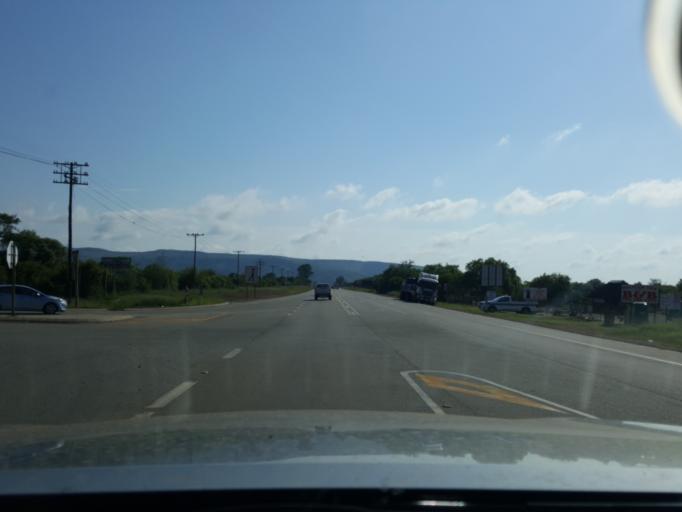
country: ZA
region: North-West
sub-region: Ngaka Modiri Molema District Municipality
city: Zeerust
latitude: -25.5607
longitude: 26.0622
